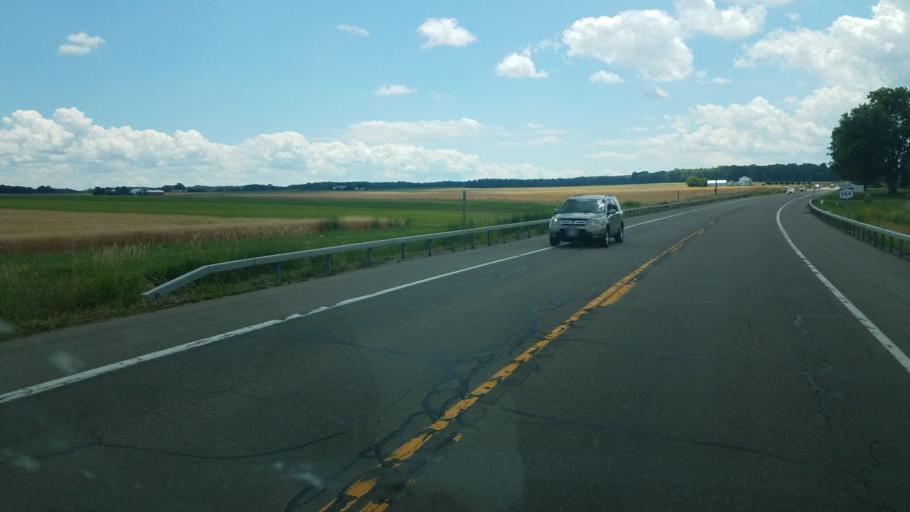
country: US
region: New York
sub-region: Yates County
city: Penn Yan
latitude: 42.6339
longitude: -77.0401
